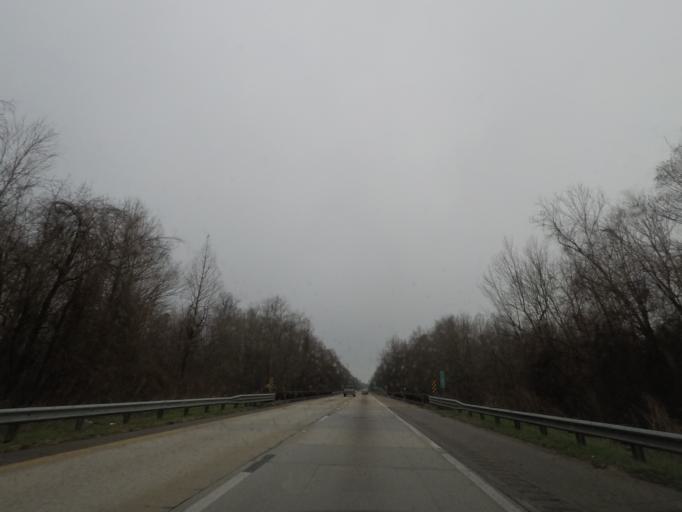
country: US
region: South Carolina
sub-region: Clarendon County
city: Manning
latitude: 33.7305
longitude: -80.2206
